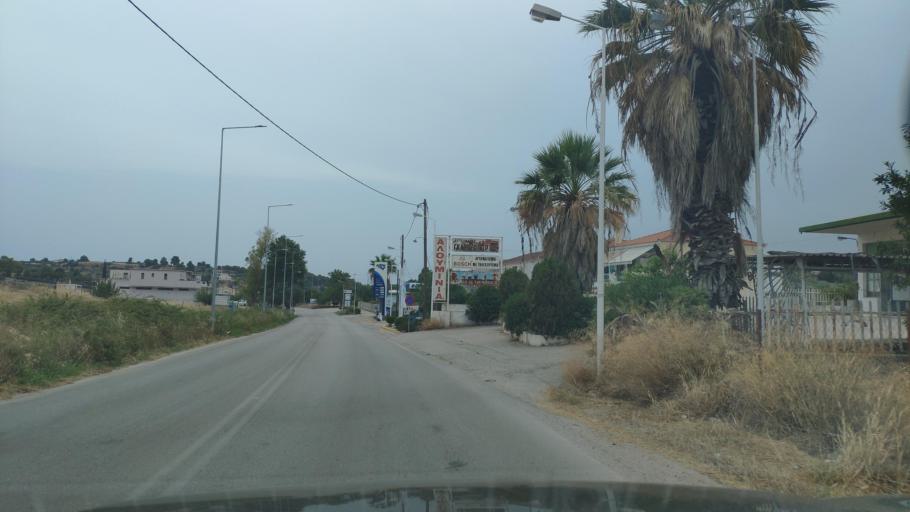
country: GR
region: Peloponnese
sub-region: Nomos Argolidos
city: Kranidi
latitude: 37.3669
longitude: 23.1620
